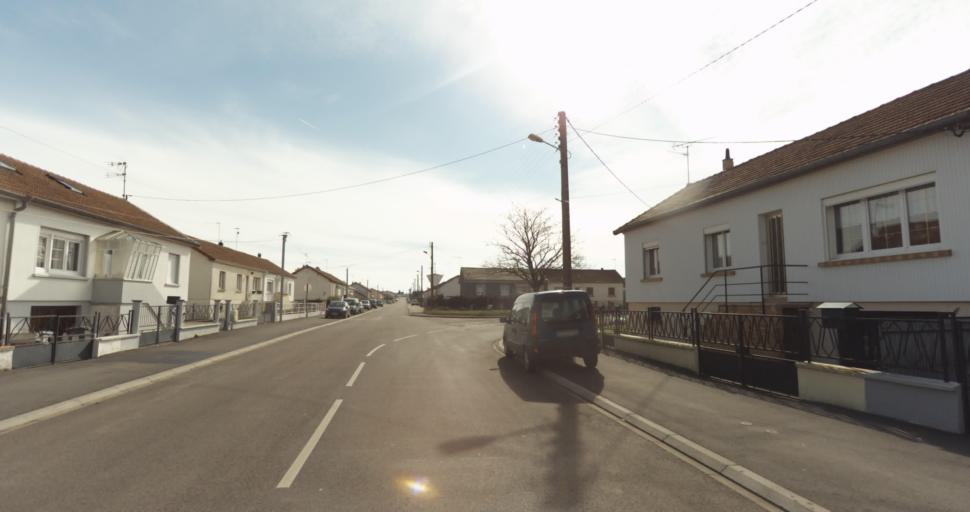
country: FR
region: Lorraine
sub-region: Departement de Meurthe-et-Moselle
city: Jarny
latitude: 49.1560
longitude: 5.8779
